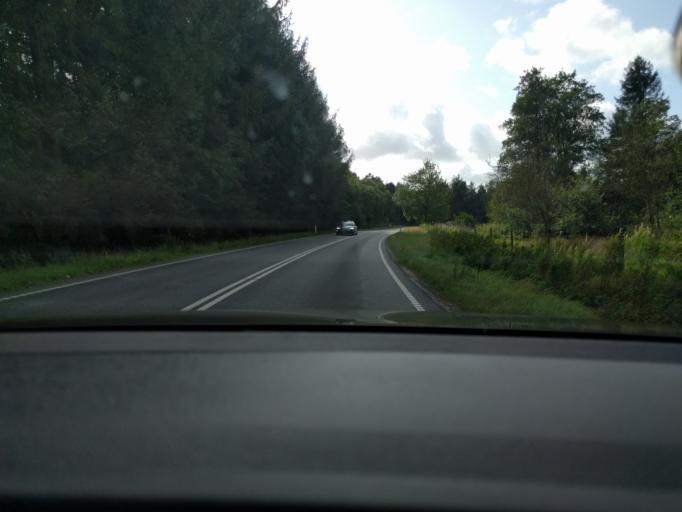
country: DK
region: Central Jutland
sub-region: Viborg Kommune
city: Bjerringbro
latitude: 56.2850
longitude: 9.6479
